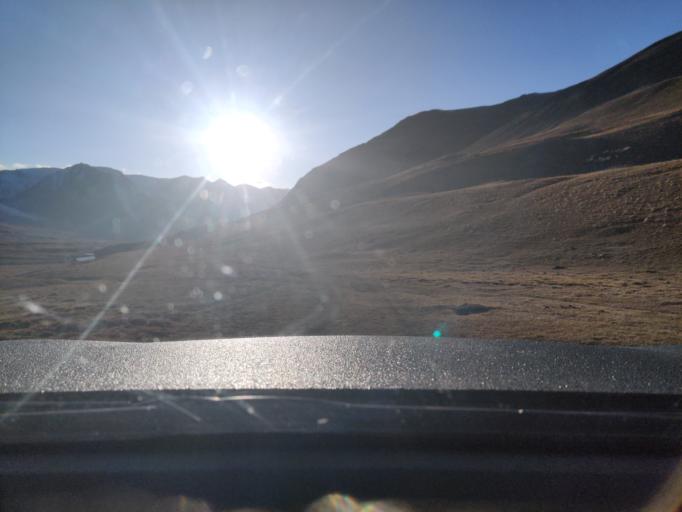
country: KG
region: Ysyk-Koel
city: Kadzhi-Say
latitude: 41.7602
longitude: 77.4336
